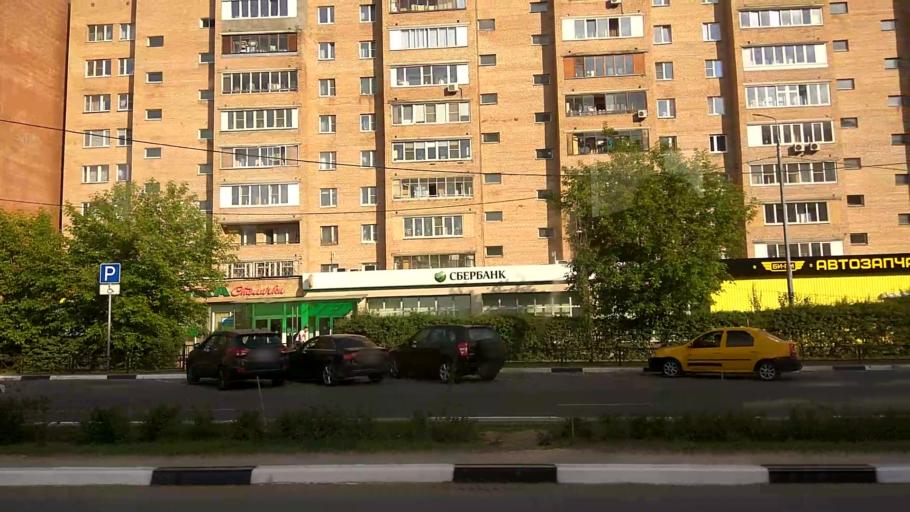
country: RU
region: Moskovskaya
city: Mytishchi
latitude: 55.9156
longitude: 37.7223
